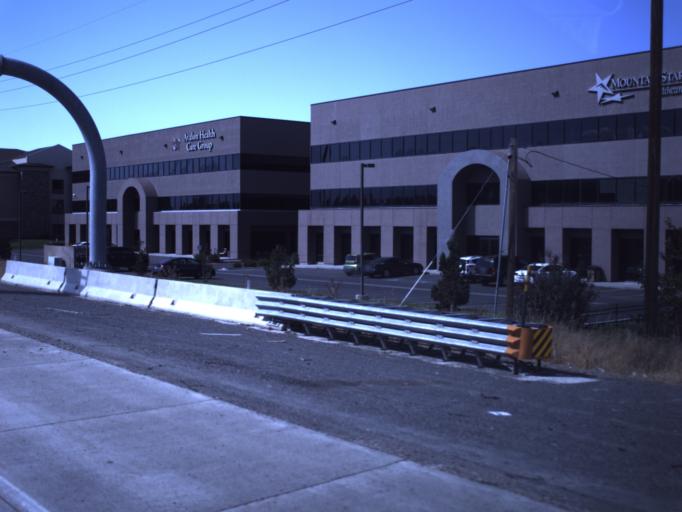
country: US
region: Utah
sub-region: Salt Lake County
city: Salt Lake City
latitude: 40.7754
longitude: -111.9494
